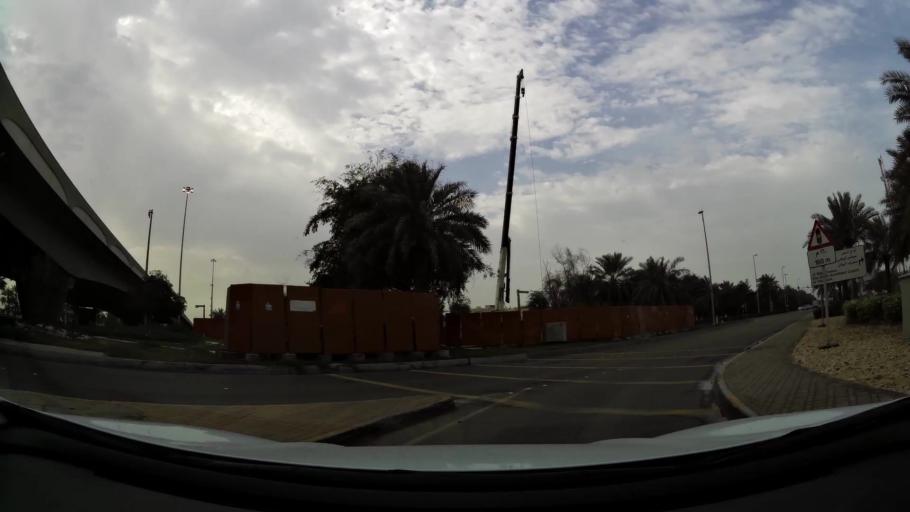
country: AE
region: Abu Dhabi
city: Abu Dhabi
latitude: 24.4557
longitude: 54.4027
